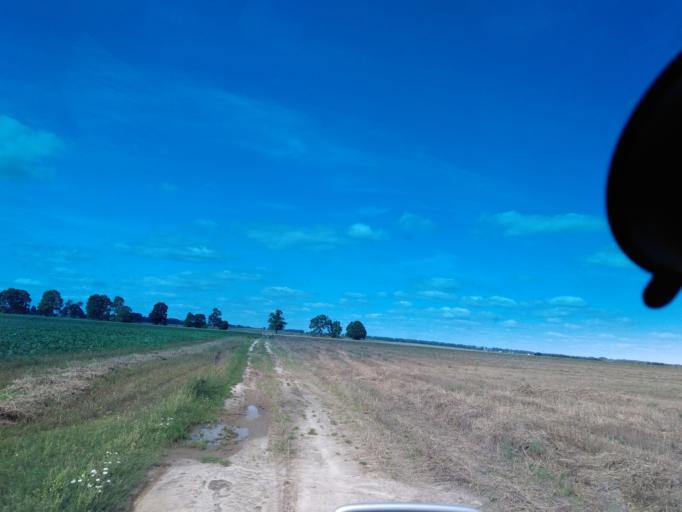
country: BY
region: Minsk
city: Stan'kava
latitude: 53.6312
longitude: 27.3269
